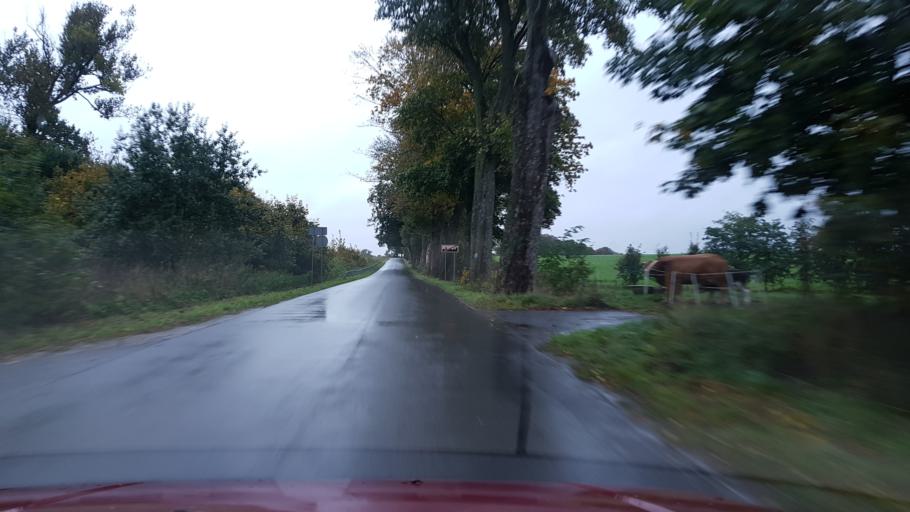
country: PL
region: West Pomeranian Voivodeship
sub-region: Koszalin
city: Koszalin
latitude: 54.1369
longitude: 16.1162
